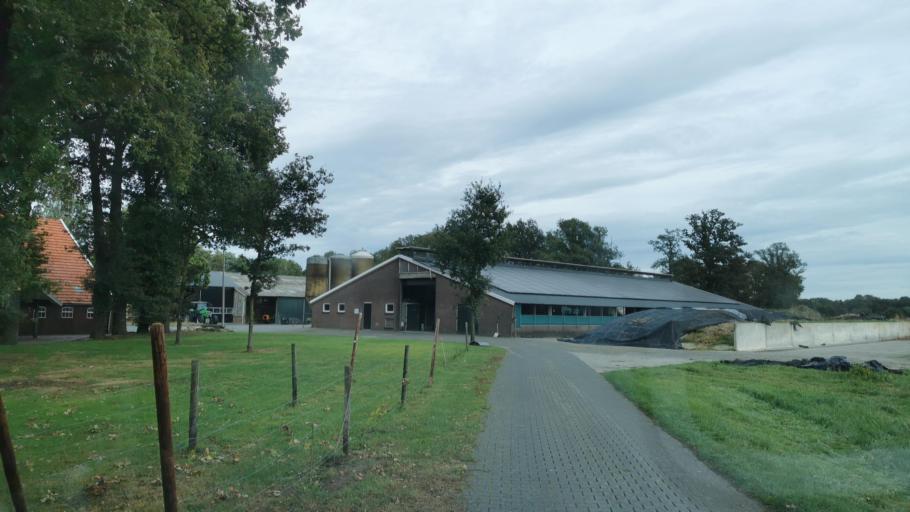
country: NL
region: Overijssel
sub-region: Gemeente Losser
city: Losser
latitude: 52.3281
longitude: 7.0141
